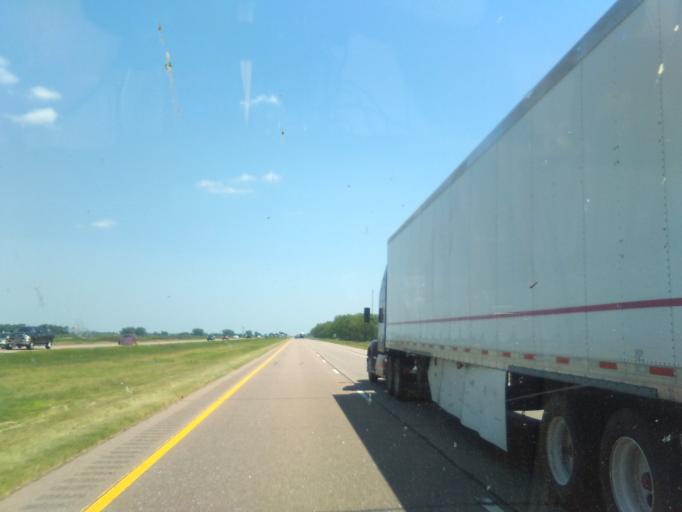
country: US
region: Nebraska
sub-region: Dawson County
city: Cozad
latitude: 40.8795
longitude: -100.0715
